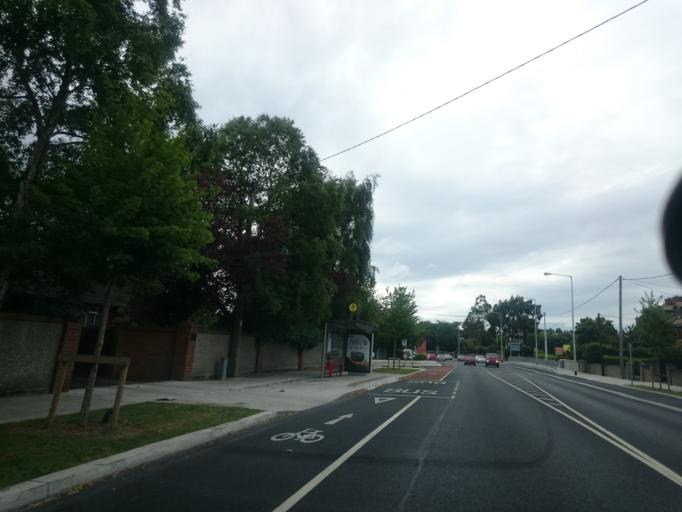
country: IE
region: Leinster
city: Dundrum
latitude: 53.3018
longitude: -6.2653
